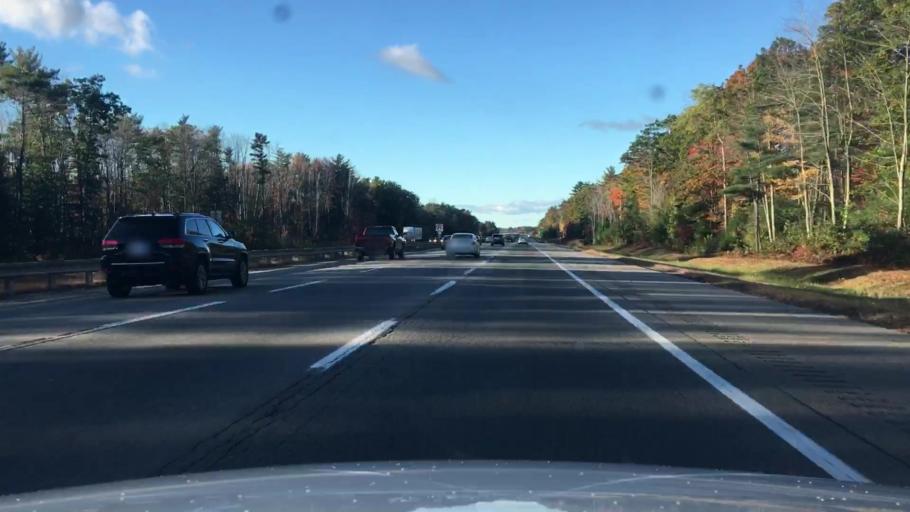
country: US
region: Maine
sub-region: York County
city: Saco
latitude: 43.5388
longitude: -70.4413
